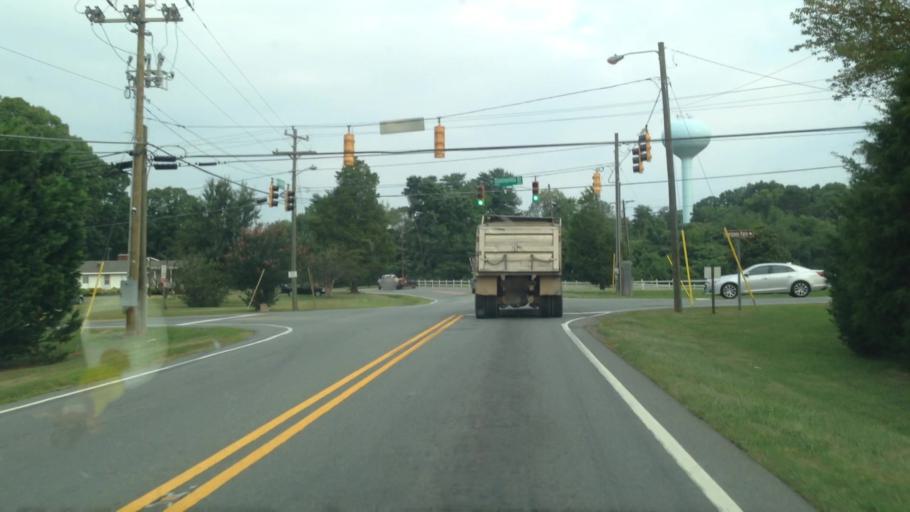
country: US
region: North Carolina
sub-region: Forsyth County
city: Rural Hall
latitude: 36.1997
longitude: -80.2738
